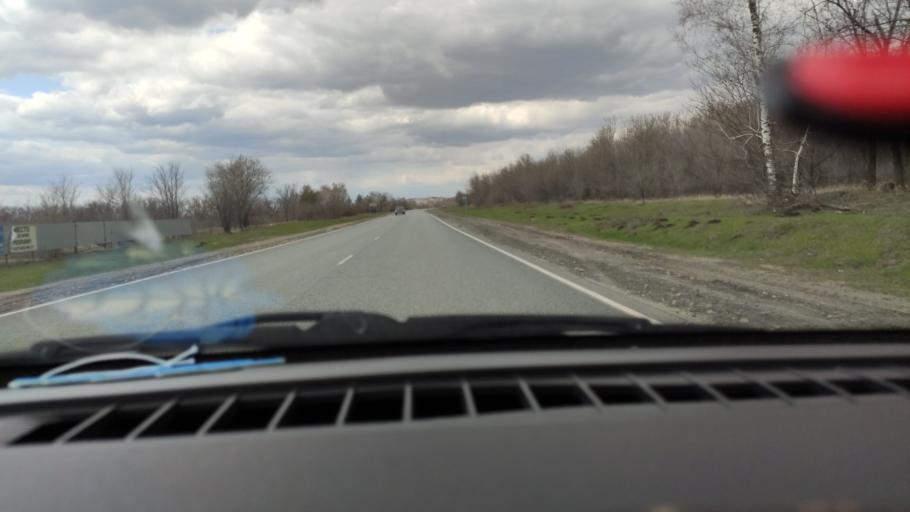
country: RU
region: Saratov
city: Tersa
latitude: 52.0825
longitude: 47.5679
